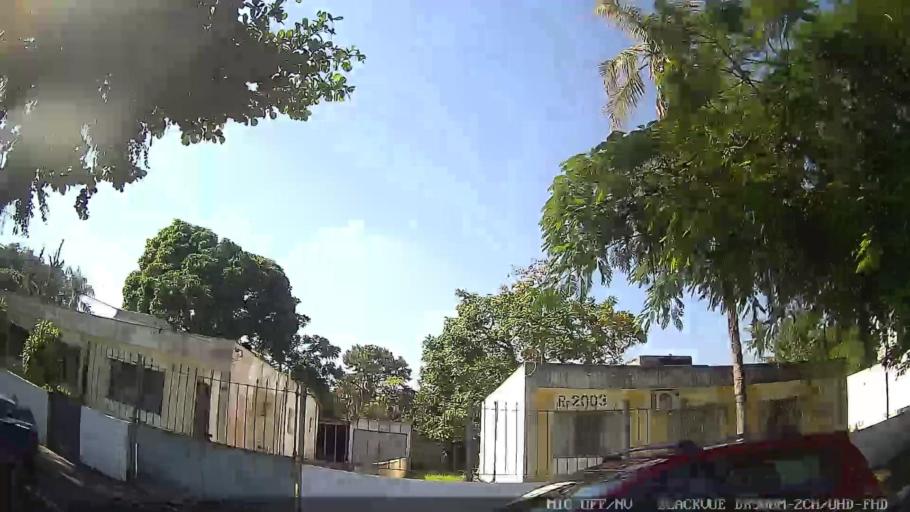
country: BR
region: Sao Paulo
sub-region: Santos
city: Santos
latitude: -23.9342
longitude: -46.3044
